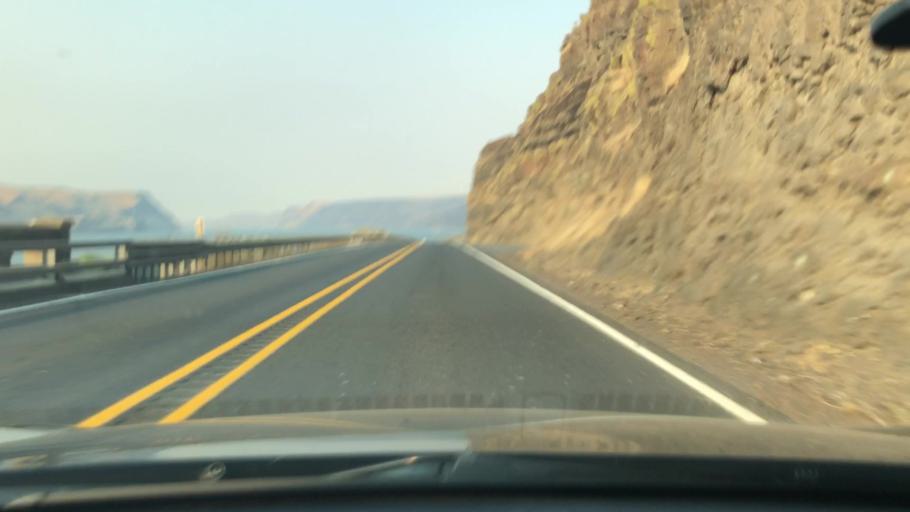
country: US
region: Washington
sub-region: Benton County
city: Highland
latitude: 45.9503
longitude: -119.0599
